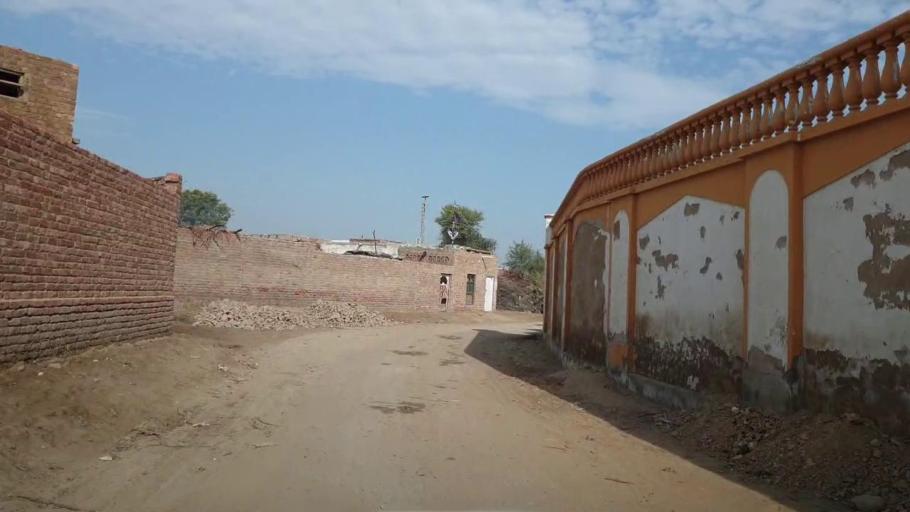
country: PK
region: Sindh
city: Matiari
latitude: 25.6061
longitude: 68.5074
